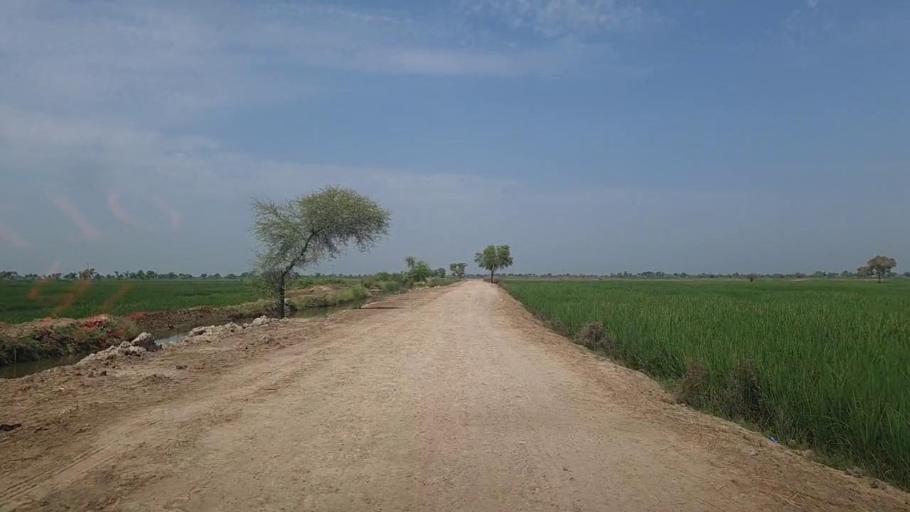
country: PK
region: Sindh
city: Thul
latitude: 28.2968
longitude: 68.6800
